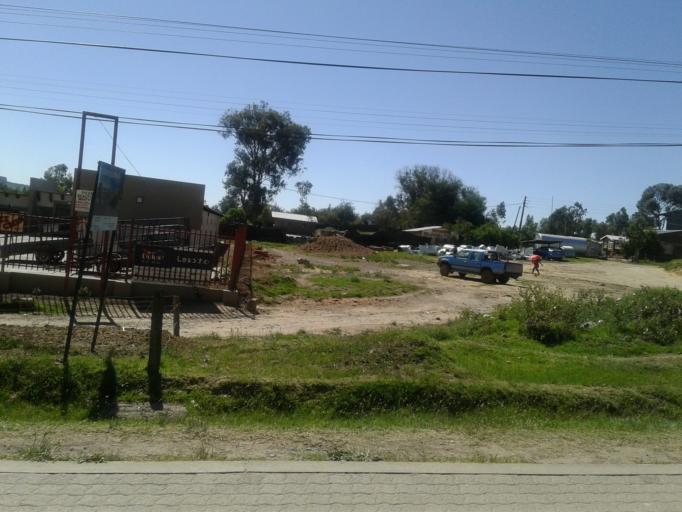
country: LS
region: Butha-Buthe
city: Butha-Buthe
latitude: -28.7636
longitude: 28.2550
